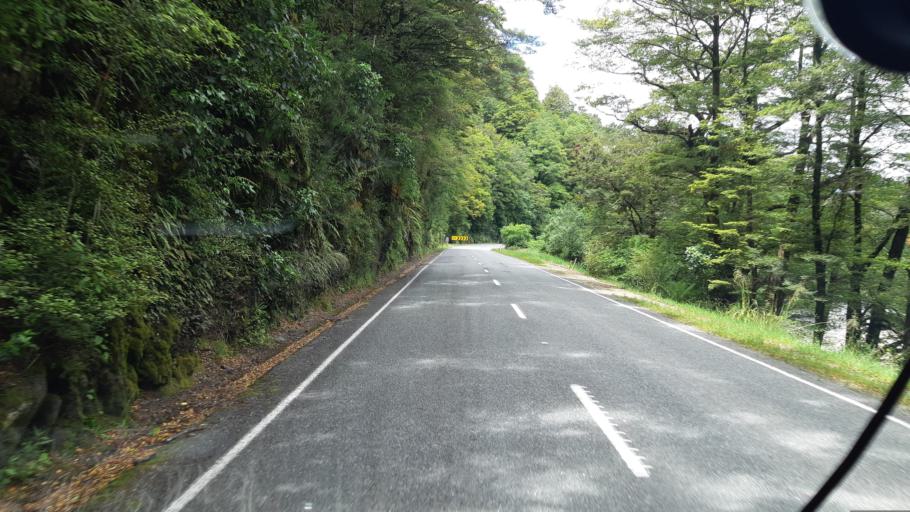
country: NZ
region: West Coast
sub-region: Buller District
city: Westport
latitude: -42.1358
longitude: 171.8856
